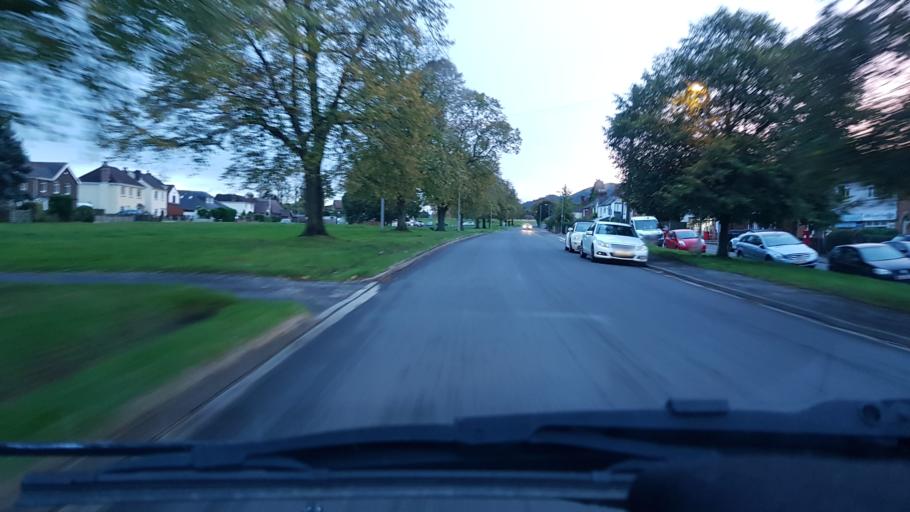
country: GB
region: England
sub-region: Worcestershire
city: Great Malvern
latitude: 52.1024
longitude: -2.3060
